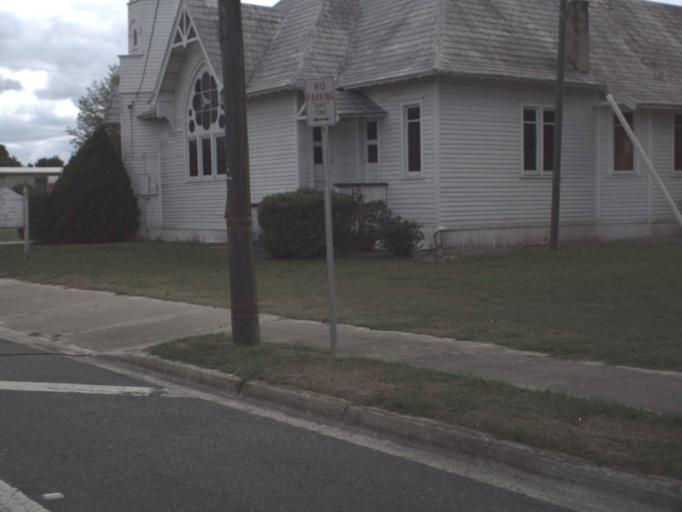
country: US
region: Florida
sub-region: Marion County
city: Citra
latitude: 29.4159
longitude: -82.1101
